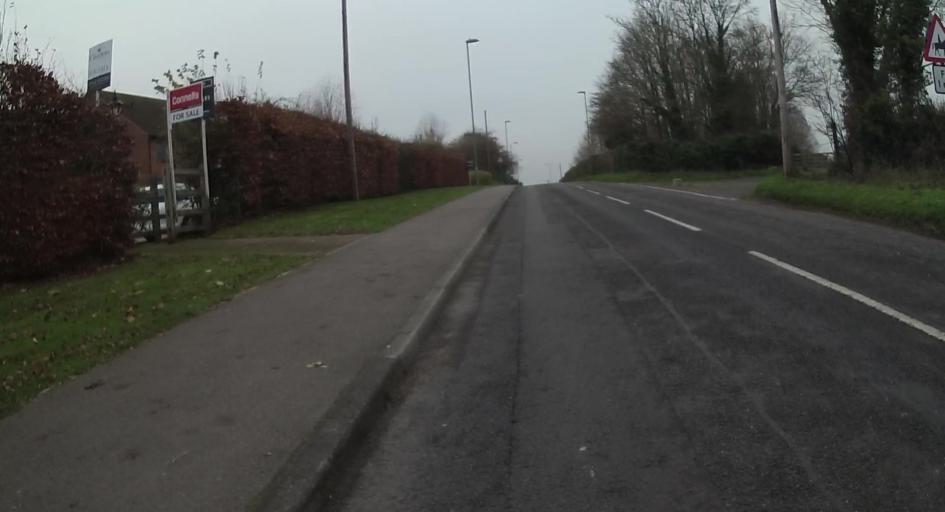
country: GB
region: England
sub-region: Hampshire
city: Kings Worthy
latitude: 51.0983
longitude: -1.2952
